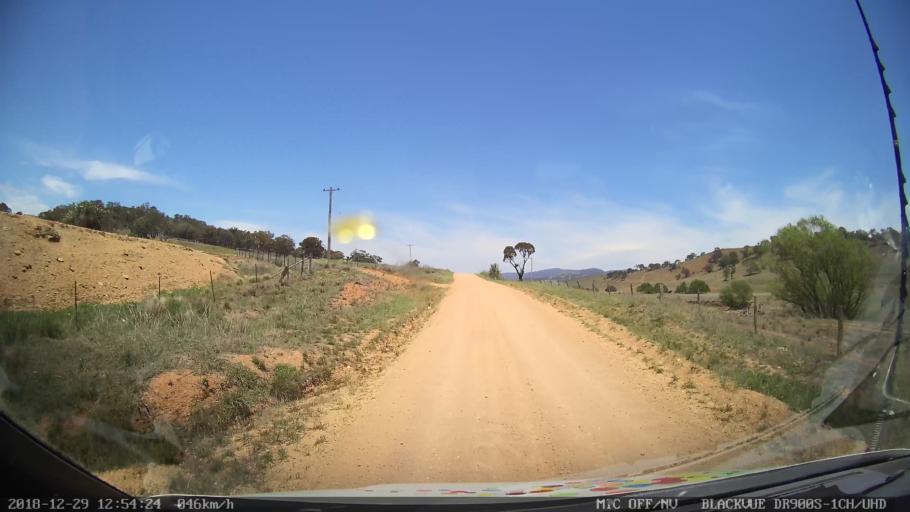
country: AU
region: Australian Capital Territory
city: Macarthur
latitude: -35.6912
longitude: 149.1876
